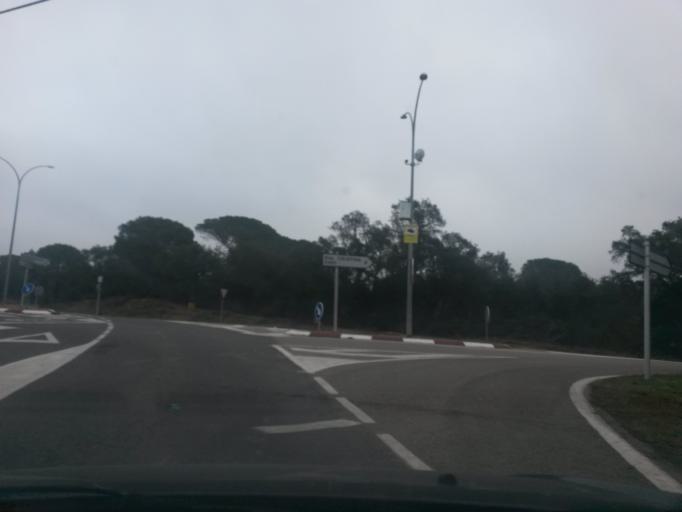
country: ES
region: Catalonia
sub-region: Provincia de Girona
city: Santa Cristina d'Aro
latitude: 41.8534
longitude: 2.9739
